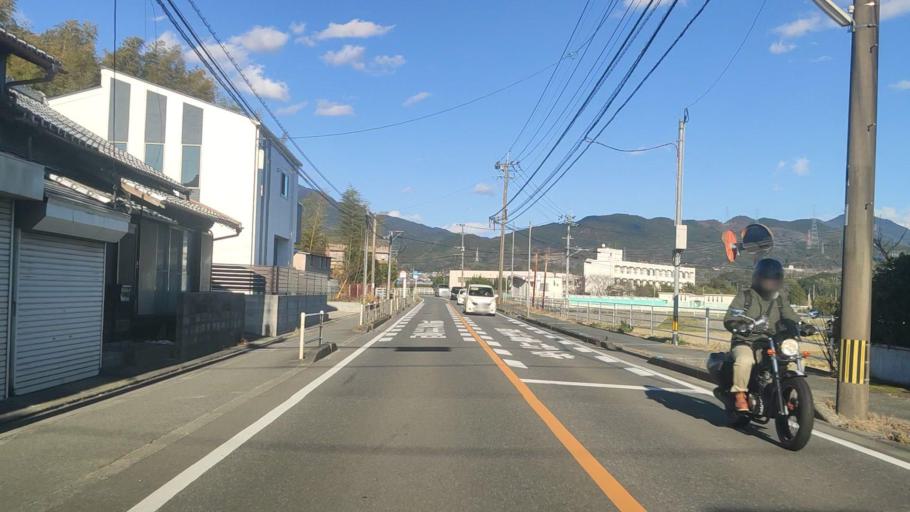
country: JP
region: Fukuoka
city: Dazaifu
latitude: 33.4979
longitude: 130.5479
